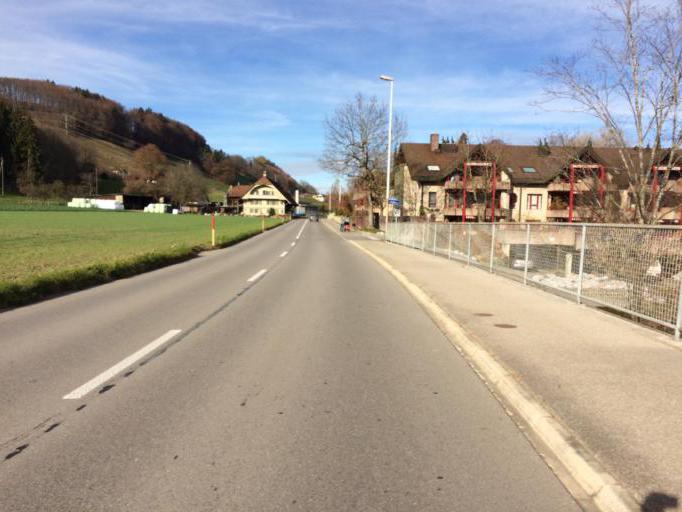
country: CH
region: Bern
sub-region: Bern-Mittelland District
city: Belp
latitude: 46.8949
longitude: 7.4917
